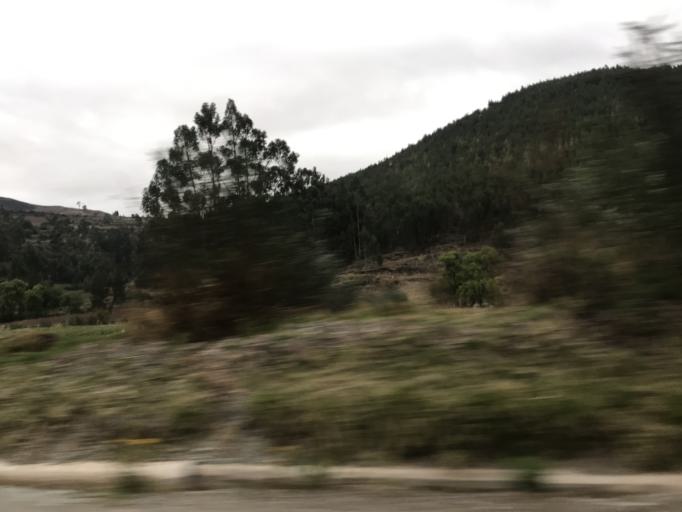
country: PE
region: Cusco
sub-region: Provincia de Anta
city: Huarocondo
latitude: -13.4012
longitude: -72.2099
